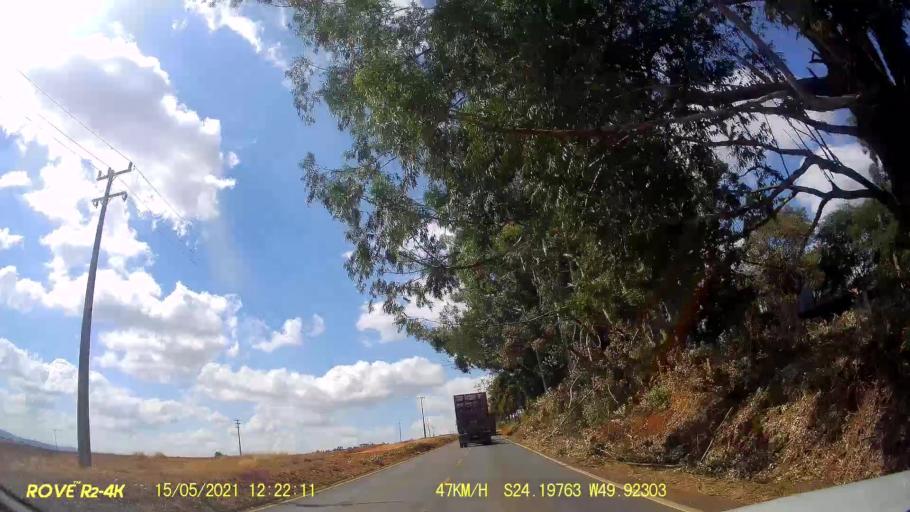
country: BR
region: Parana
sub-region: Jaguariaiva
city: Jaguariaiva
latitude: -24.1976
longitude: -49.9229
